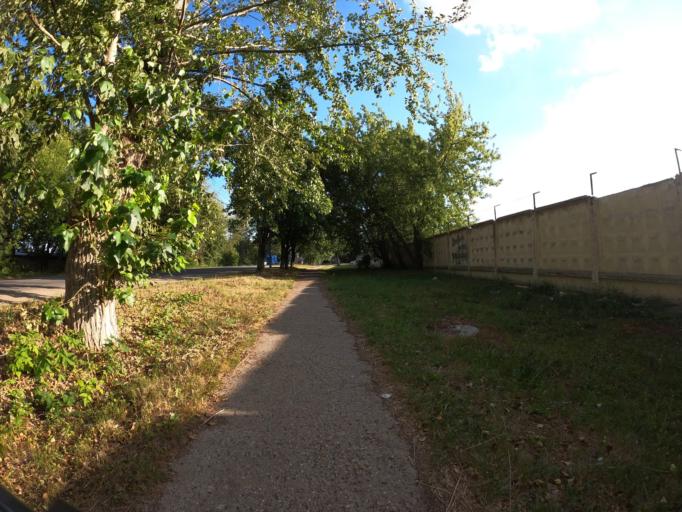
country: RU
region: Moskovskaya
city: Raduzhnyy
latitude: 55.1395
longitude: 38.7314
